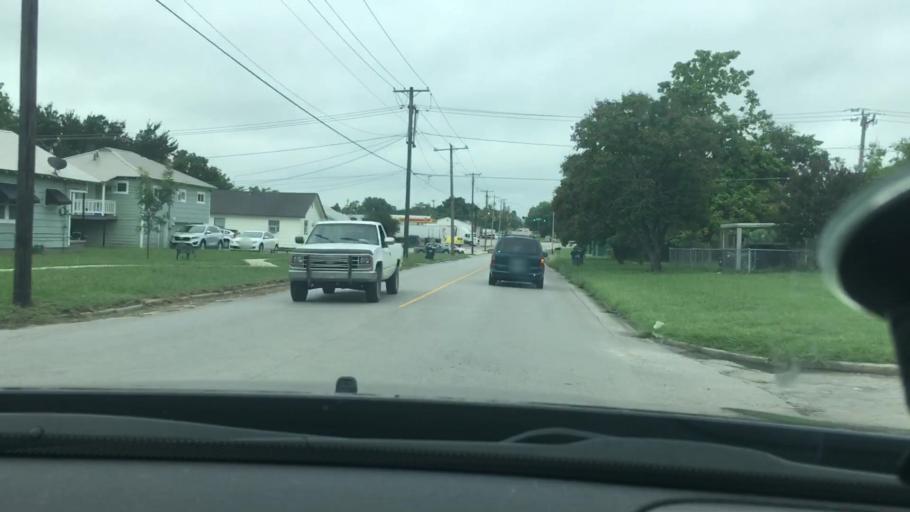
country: US
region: Oklahoma
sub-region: Pontotoc County
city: Ada
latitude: 34.7767
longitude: -96.6867
